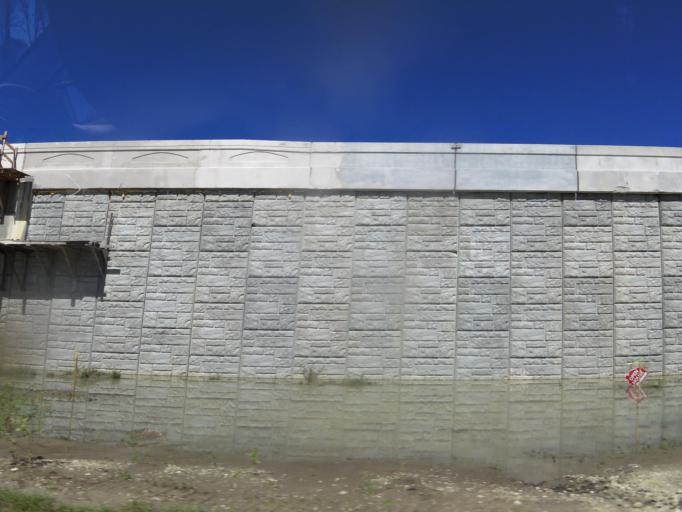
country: US
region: Florida
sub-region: Seminole County
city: Heathrow
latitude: 28.8152
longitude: -81.4259
